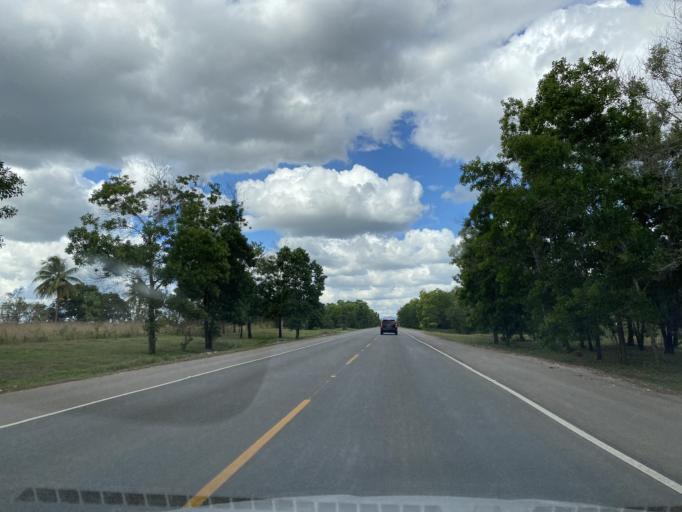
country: DO
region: Santo Domingo
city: Guerra
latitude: 18.6740
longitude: -69.7441
